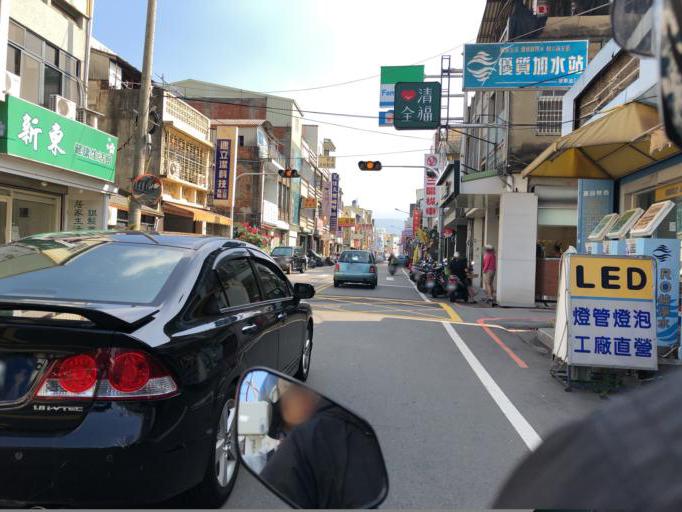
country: TW
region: Taiwan
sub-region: Miaoli
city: Miaoli
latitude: 24.5513
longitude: 120.8210
